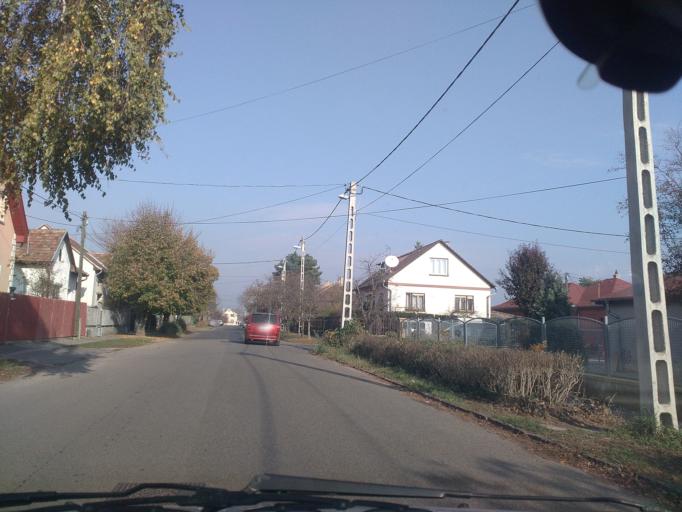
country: HU
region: Budapest
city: Budapest XVIII. keruelet
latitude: 47.4380
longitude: 19.1981
